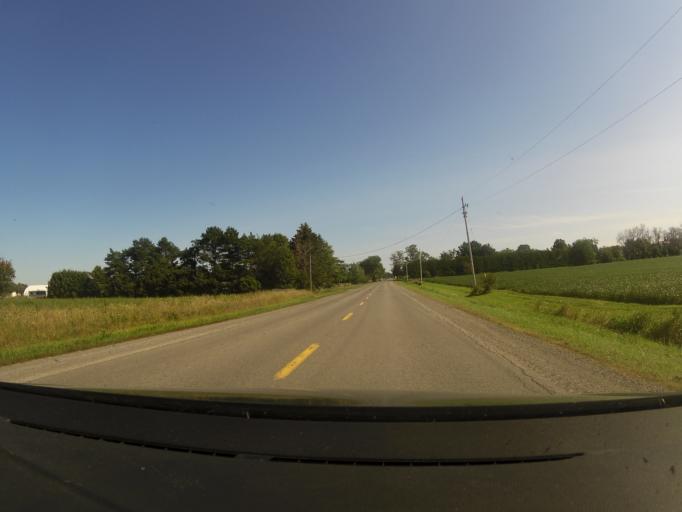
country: CA
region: Ontario
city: Carleton Place
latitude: 45.3578
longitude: -76.0969
